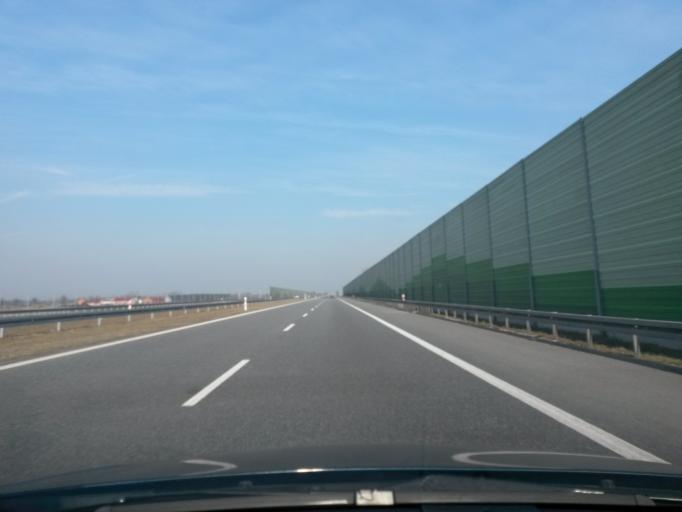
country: PL
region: Lodz Voivodeship
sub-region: Powiat leczycki
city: Piatek
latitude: 52.0855
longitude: 19.5254
